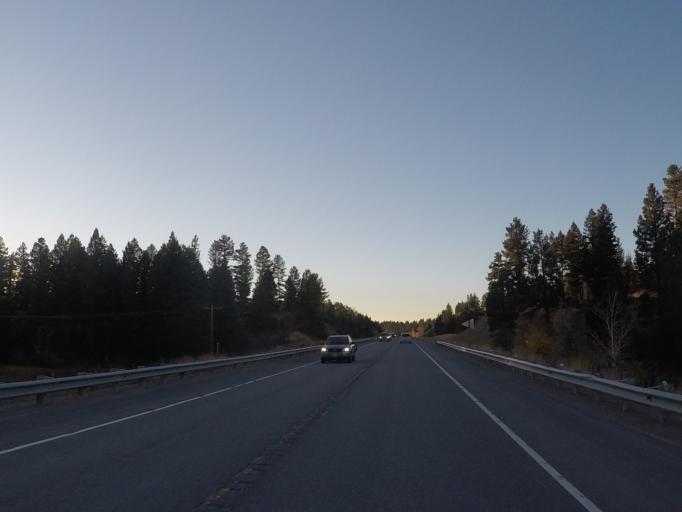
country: US
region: Montana
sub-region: Lewis and Clark County
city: Lincoln
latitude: 47.0106
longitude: -113.0617
